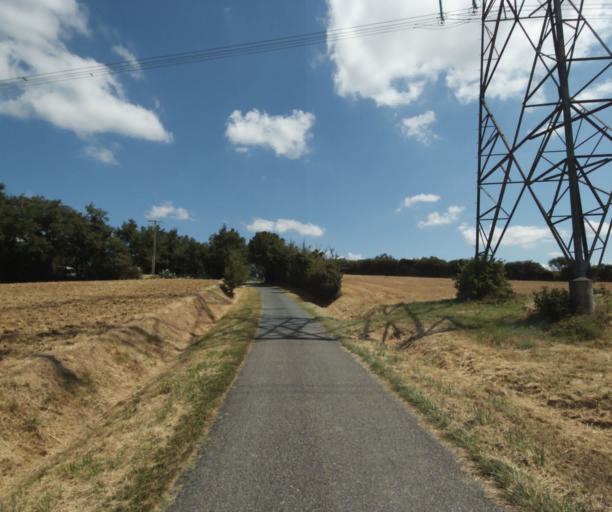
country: FR
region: Midi-Pyrenees
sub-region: Departement de la Haute-Garonne
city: Auriac-sur-Vendinelle
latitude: 43.4716
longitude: 1.8040
